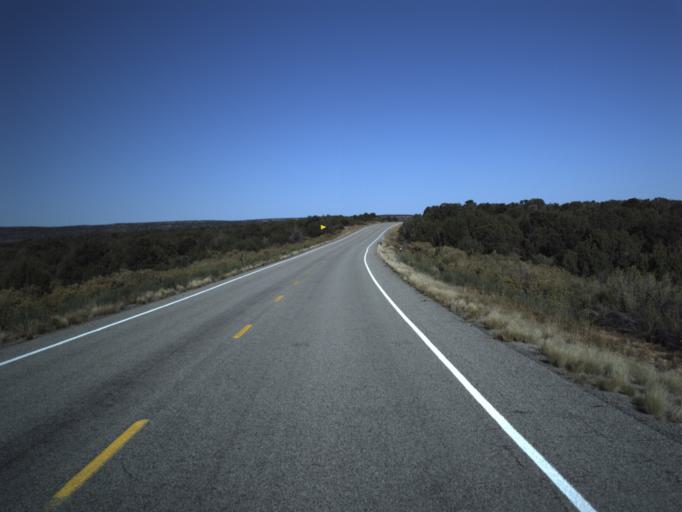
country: US
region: Utah
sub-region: San Juan County
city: Blanding
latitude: 37.5444
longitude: -109.9816
